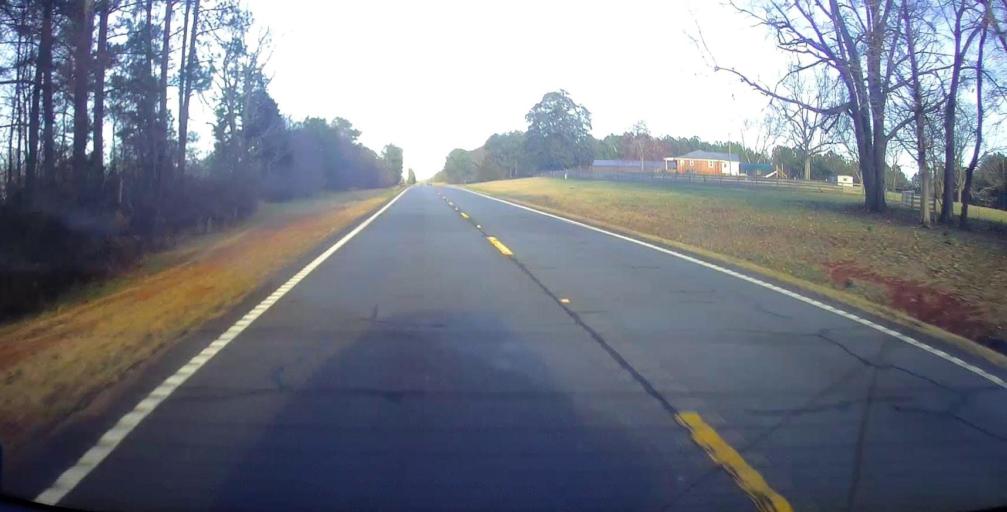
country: US
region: Georgia
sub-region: Talbot County
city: Talbotton
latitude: 32.7859
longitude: -84.5195
